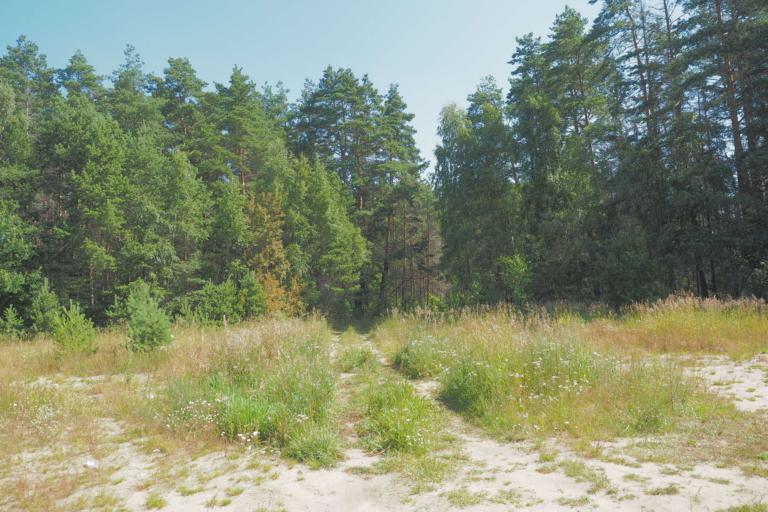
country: RU
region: Moskovskaya
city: Malyshevo
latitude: 55.5374
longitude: 38.3475
